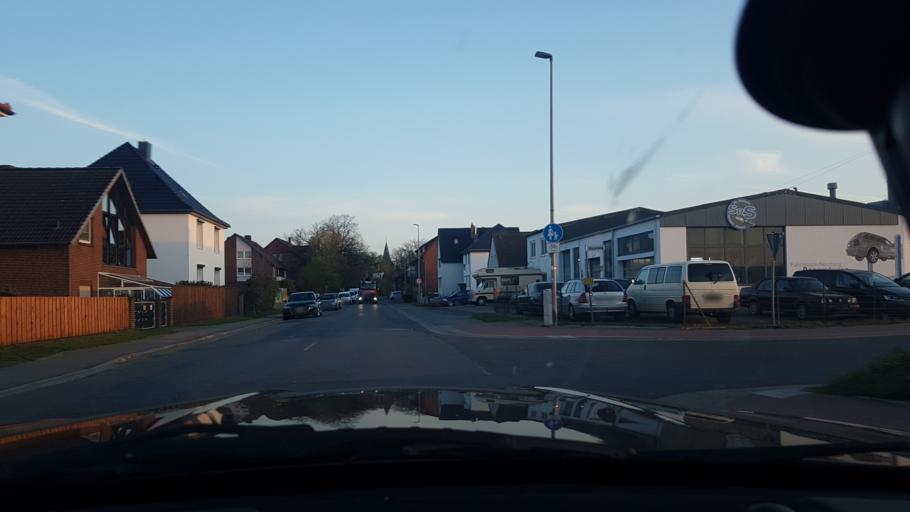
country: DE
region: Lower Saxony
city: Hemmingen
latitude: 52.2838
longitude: 9.7127
